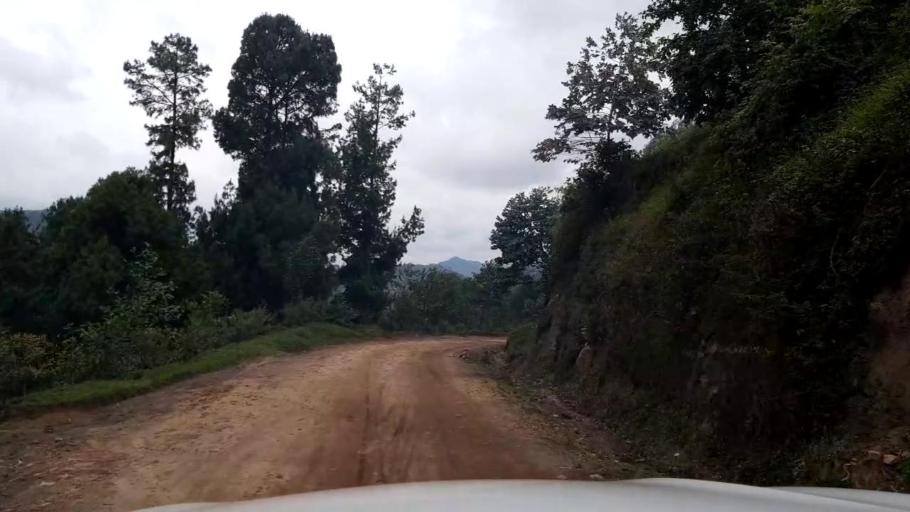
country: RW
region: Western Province
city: Kibuye
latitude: -1.9531
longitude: 29.4170
